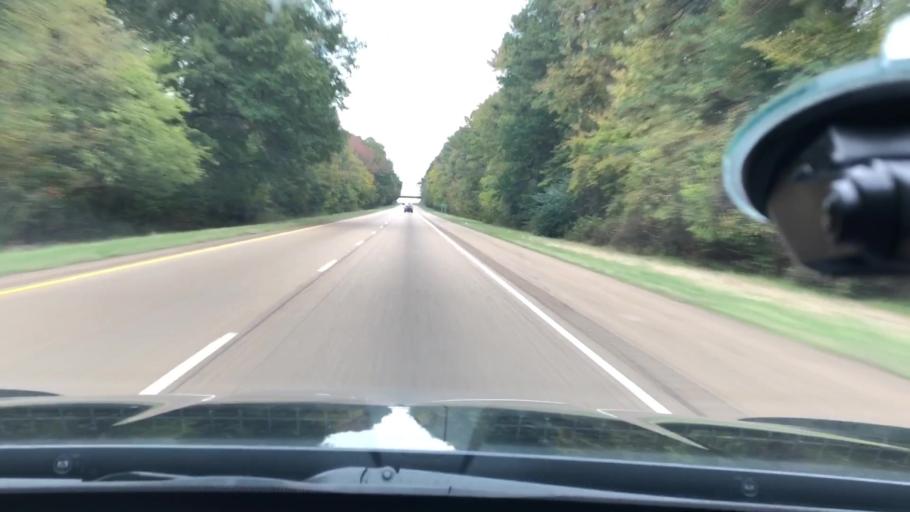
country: US
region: Arkansas
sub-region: Nevada County
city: Prescott
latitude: 33.7731
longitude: -93.4743
